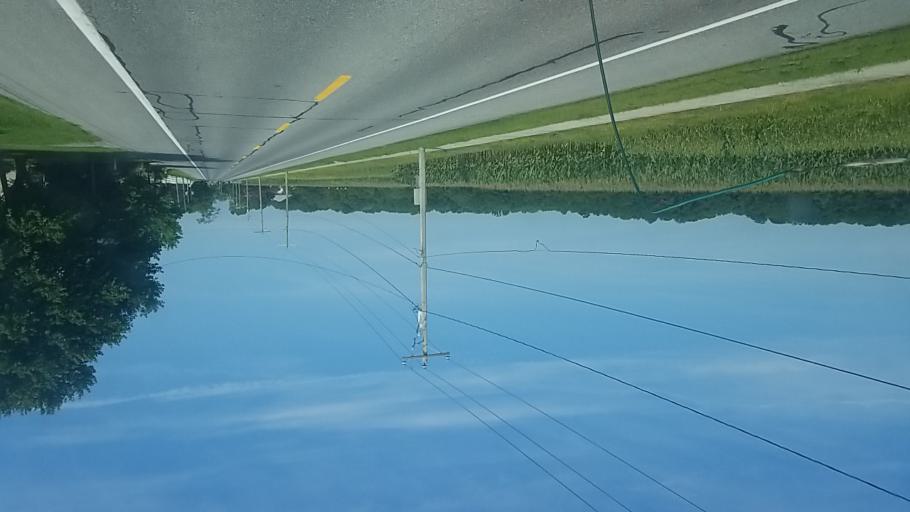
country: US
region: Delaware
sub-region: Sussex County
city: Millsboro
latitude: 38.5419
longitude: -75.2397
